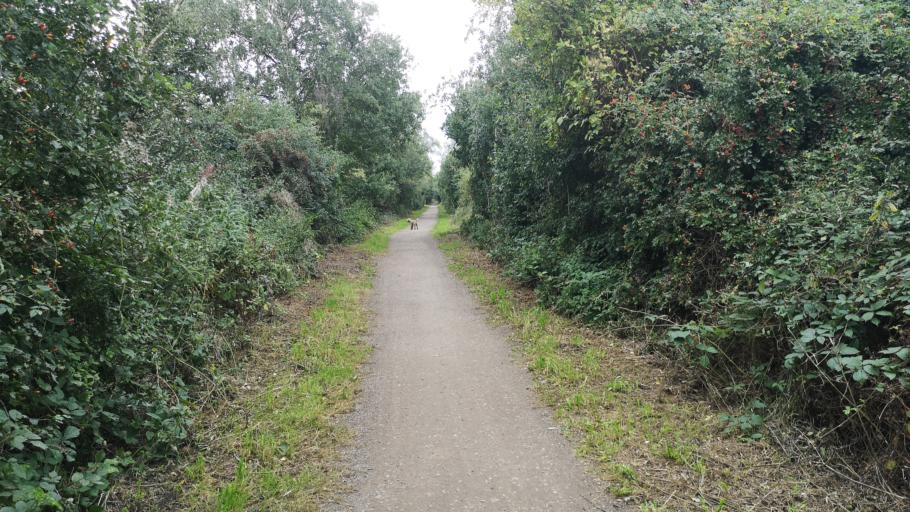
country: GB
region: England
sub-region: Barnsley
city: Royston
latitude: 53.6196
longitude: -1.4644
